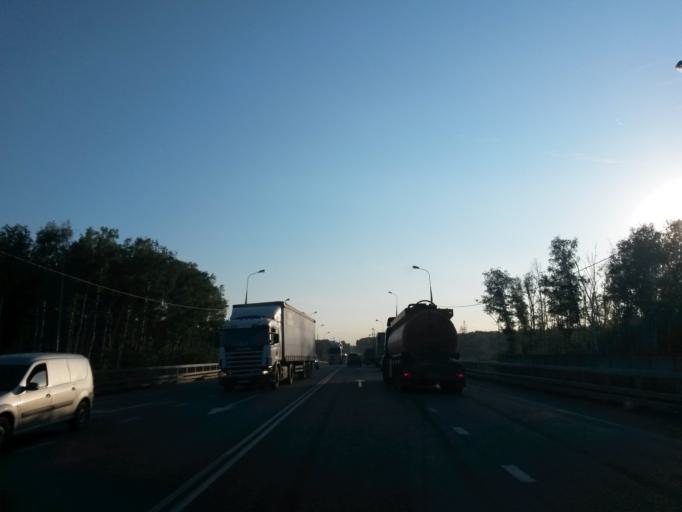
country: RU
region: Moskovskaya
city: Belyye Stolby
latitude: 55.3394
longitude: 37.8088
